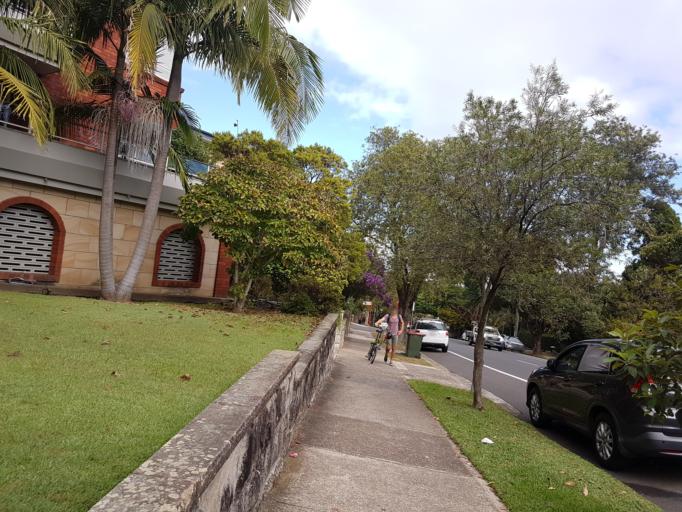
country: AU
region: New South Wales
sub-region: North Sydney
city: North Sydney
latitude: -33.8364
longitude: 151.2008
